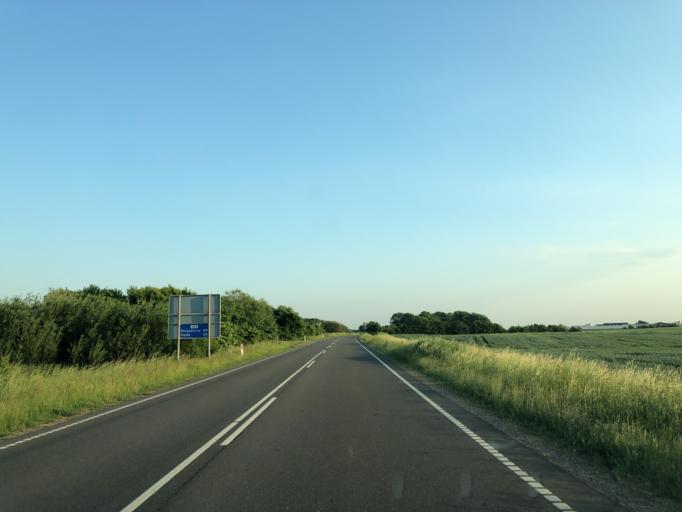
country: DK
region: Central Jutland
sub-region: Struer Kommune
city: Struer
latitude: 56.4663
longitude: 8.5466
